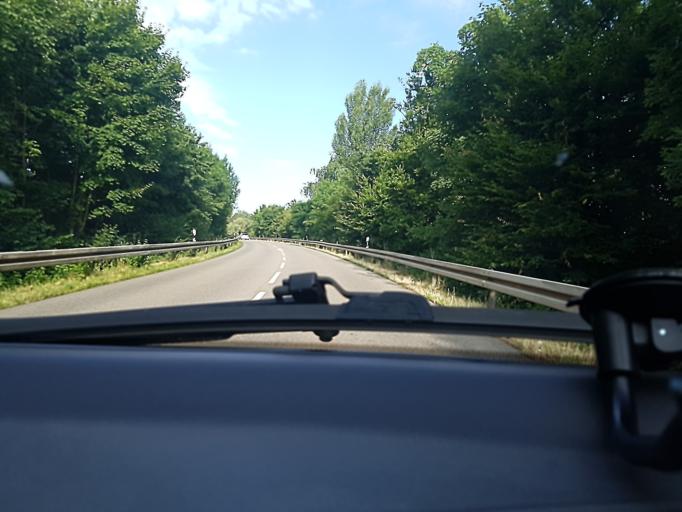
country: DE
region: Baden-Wuerttemberg
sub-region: Freiburg Region
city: Willstatt
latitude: 48.5399
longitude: 7.9118
